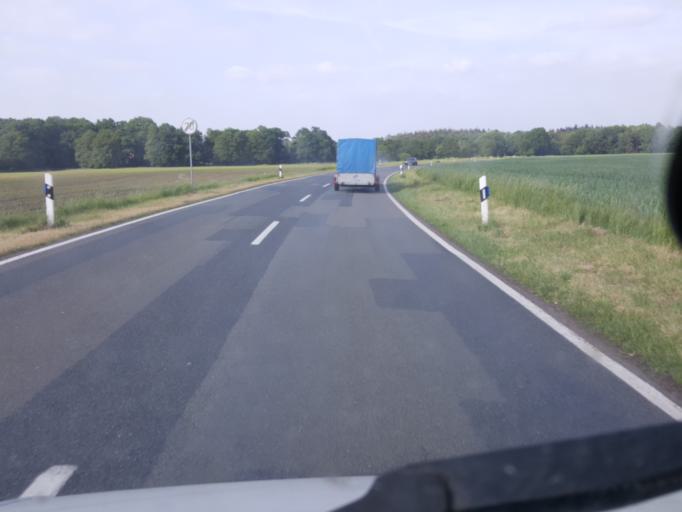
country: DE
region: Lower Saxony
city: Steyerberg
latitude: 52.5523
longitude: 8.9912
